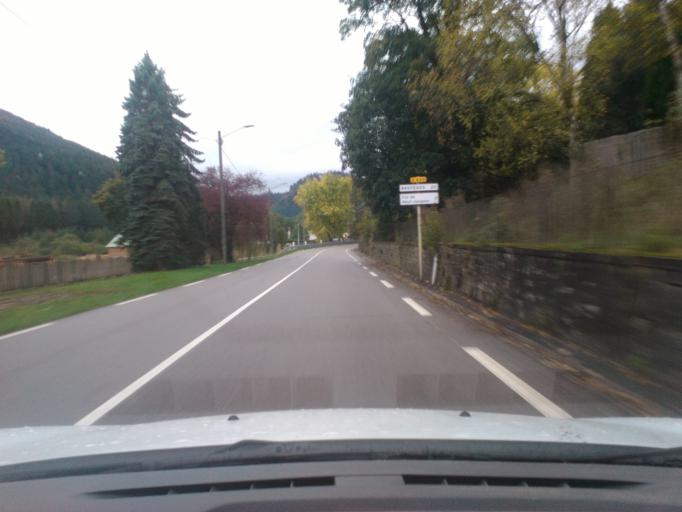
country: FR
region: Lorraine
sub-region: Departement des Vosges
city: Taintrux
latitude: 48.2737
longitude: 6.8985
